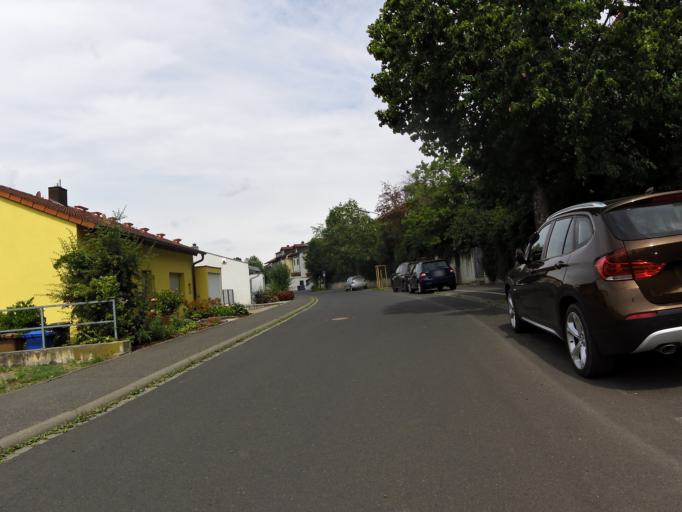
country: DE
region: Bavaria
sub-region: Regierungsbezirk Unterfranken
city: Wuerzburg
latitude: 49.7924
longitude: 9.9668
